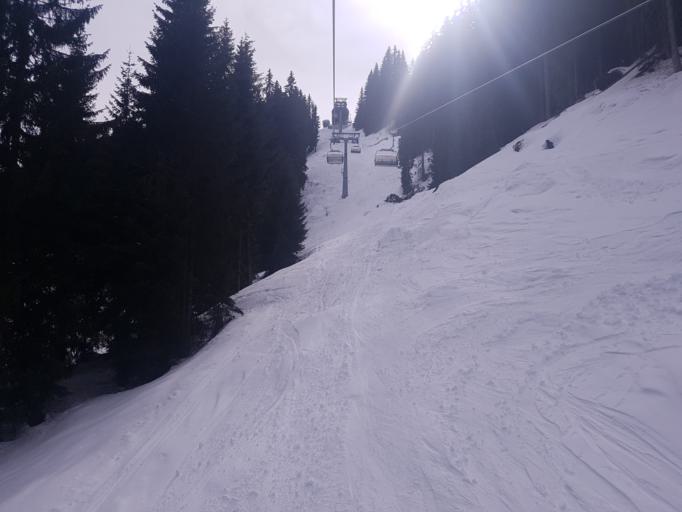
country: AT
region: Tyrol
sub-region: Politischer Bezirk Kufstein
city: Worgl
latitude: 47.4341
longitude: 12.0831
